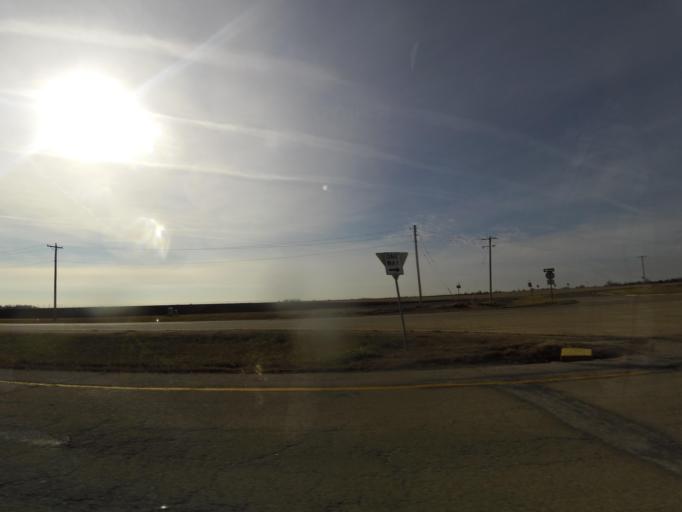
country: US
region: Illinois
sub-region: De Witt County
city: Clinton
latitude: 40.2319
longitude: -88.9703
